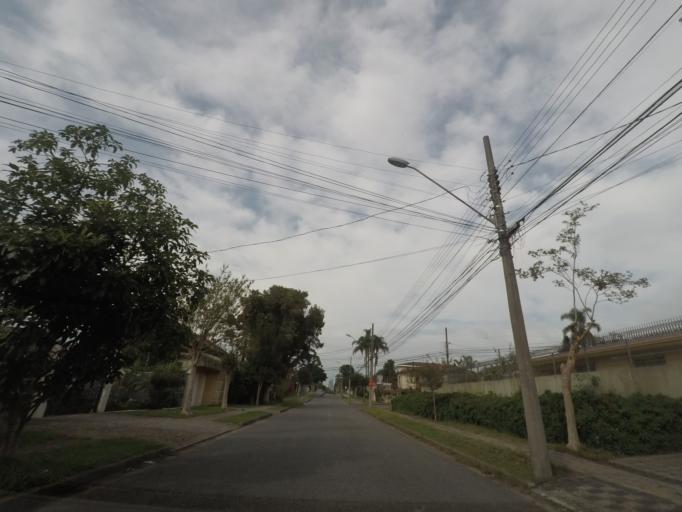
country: BR
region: Parana
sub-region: Curitiba
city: Curitiba
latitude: -25.4079
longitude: -49.2739
